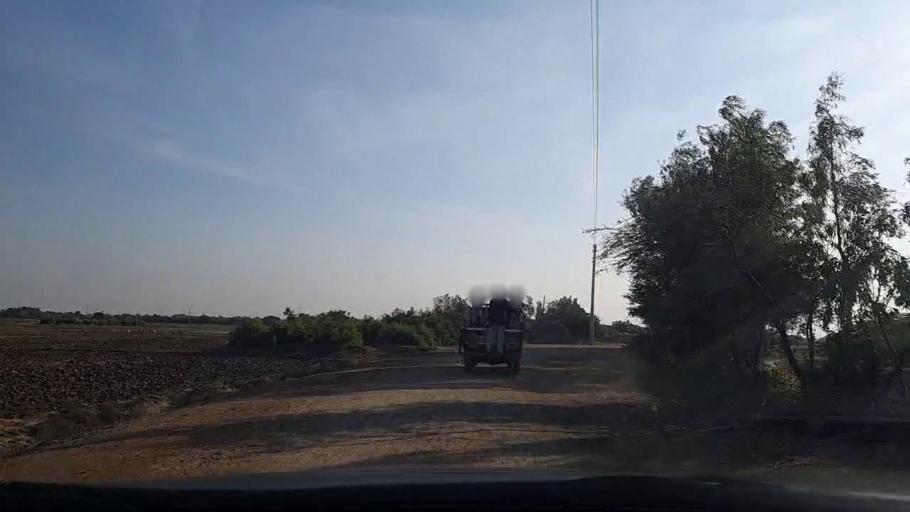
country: PK
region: Sindh
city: Mirpur Sakro
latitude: 24.5303
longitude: 67.6331
